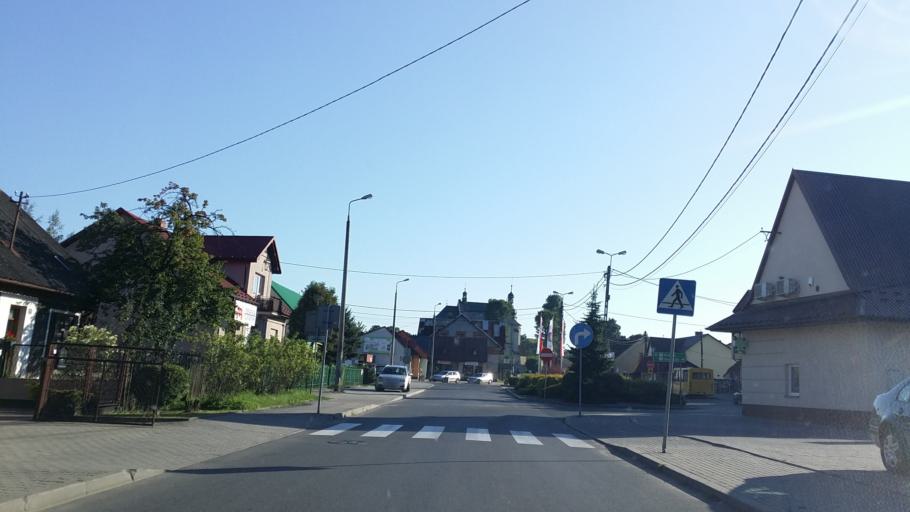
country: PL
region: Lesser Poland Voivodeship
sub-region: Powiat wadowicki
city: Spytkowice
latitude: 49.9975
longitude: 19.5118
